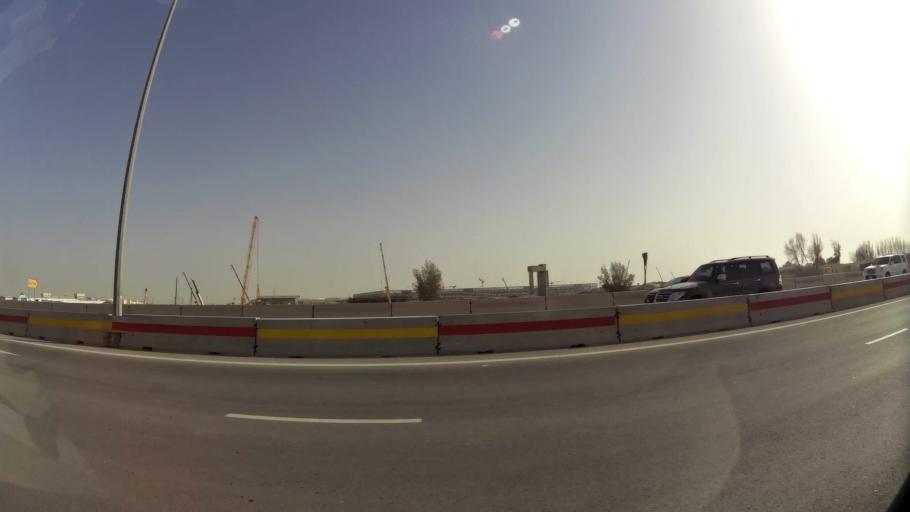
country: QA
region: Baladiyat ar Rayyan
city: Ar Rayyan
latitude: 25.3191
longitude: 51.4246
